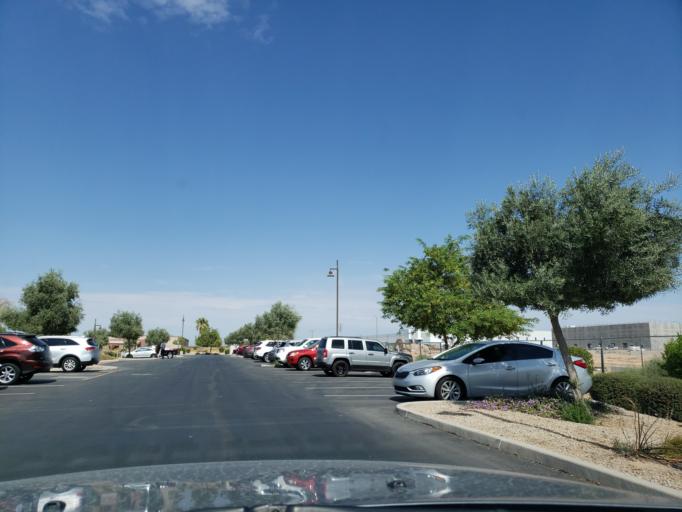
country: US
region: Arizona
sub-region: Maricopa County
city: Goodyear
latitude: 33.4391
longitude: -112.3587
